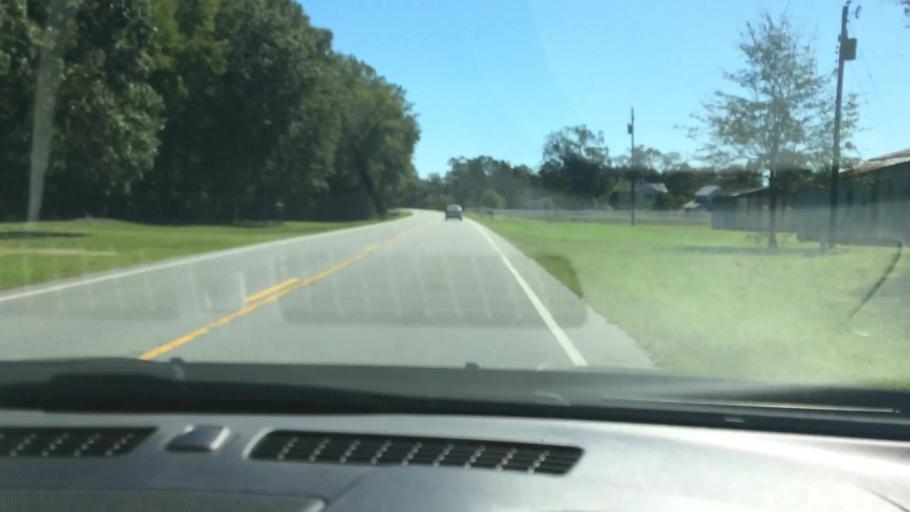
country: US
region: North Carolina
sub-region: Pitt County
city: Grifton
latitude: 35.3565
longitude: -77.3402
